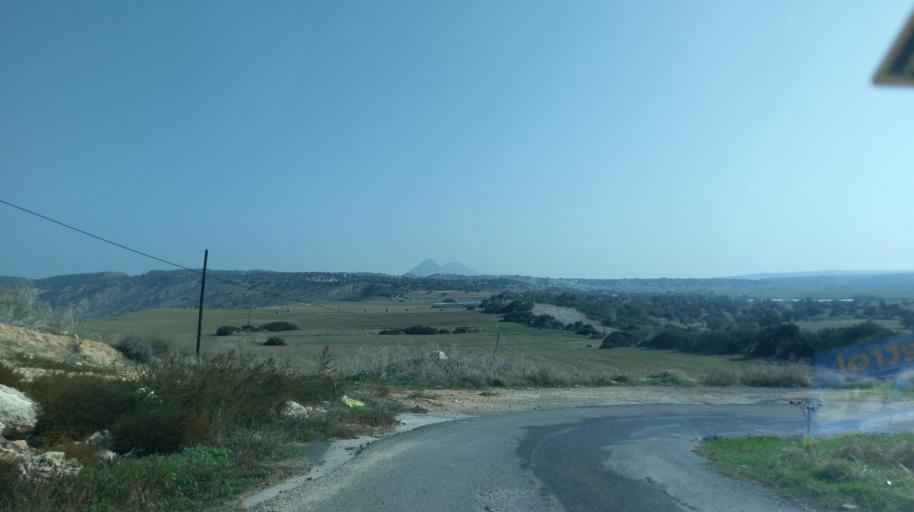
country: CY
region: Lefkosia
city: Morfou
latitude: 35.3525
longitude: 32.9827
